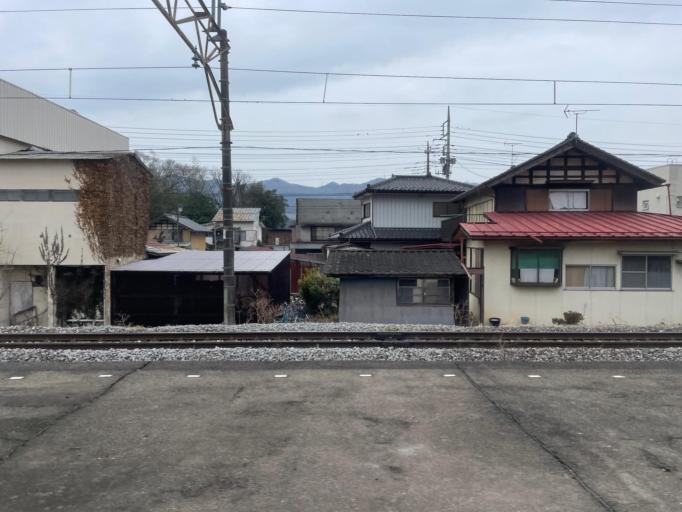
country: JP
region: Gunma
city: Numata
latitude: 36.6787
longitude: 139.0013
